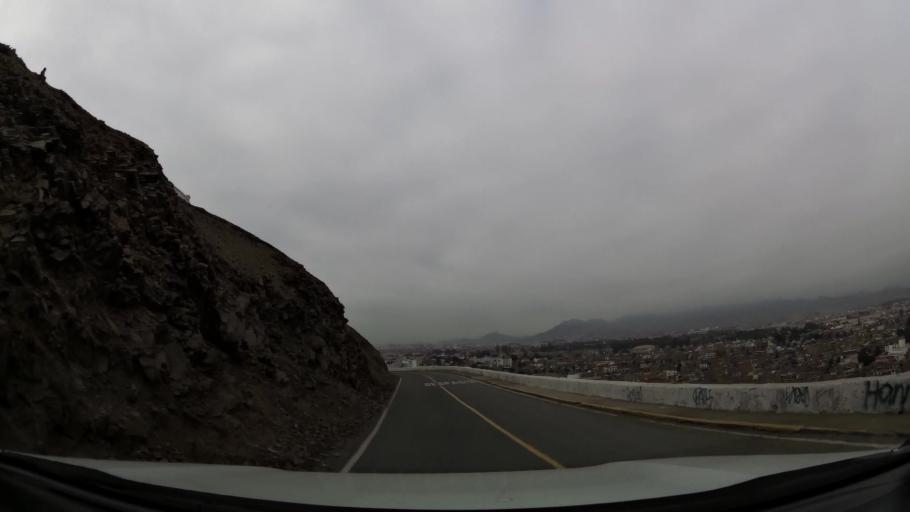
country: PE
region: Lima
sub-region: Lima
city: Surco
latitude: -12.1714
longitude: -77.0290
